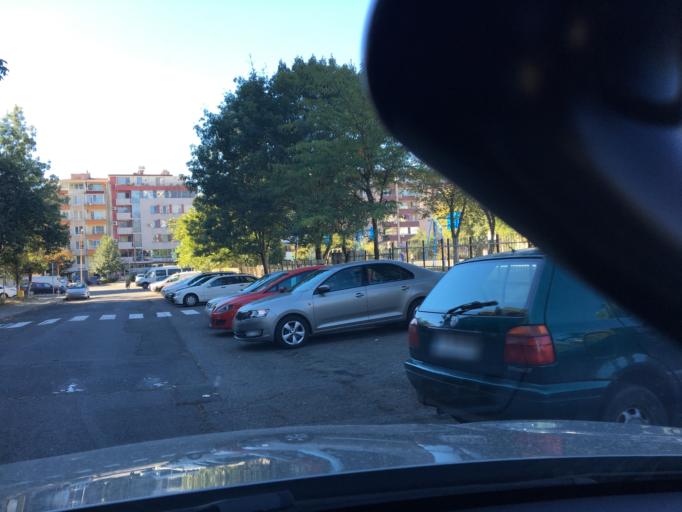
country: BG
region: Burgas
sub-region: Obshtina Burgas
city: Burgas
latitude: 42.5148
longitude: 27.4578
